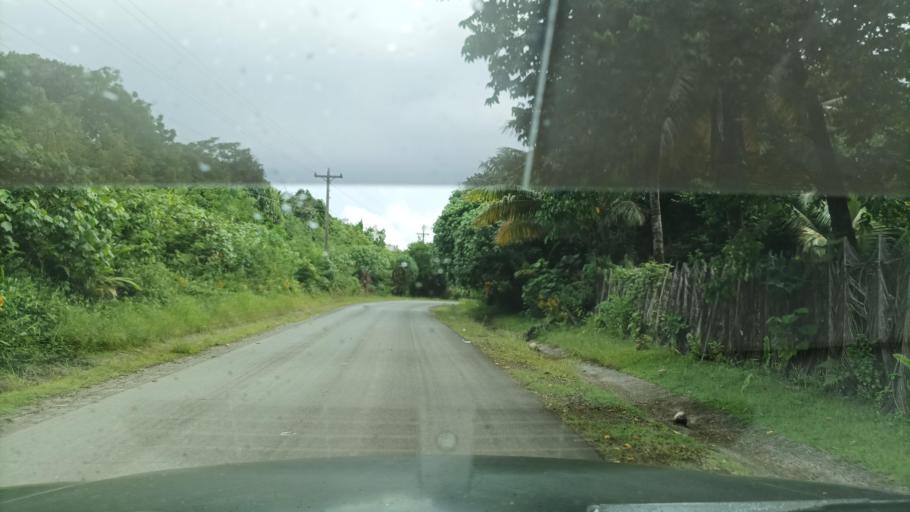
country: FM
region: Yap
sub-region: Weloy Municipality
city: Colonia
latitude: 9.5461
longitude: 138.1539
